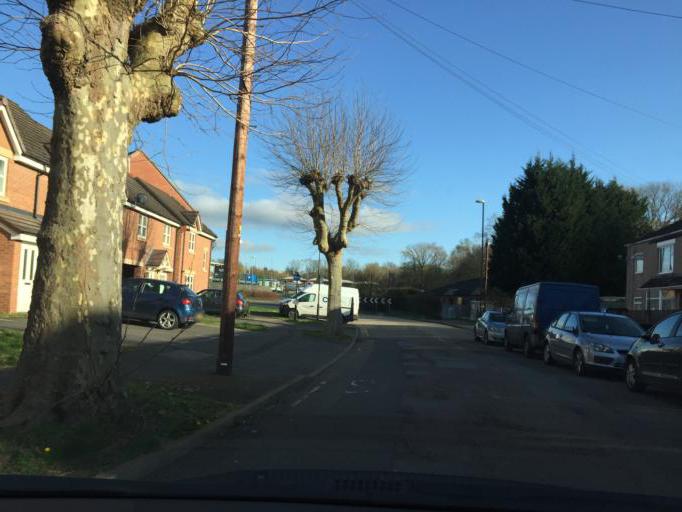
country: GB
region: England
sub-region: Coventry
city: Coventry
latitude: 52.3982
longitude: -1.4885
